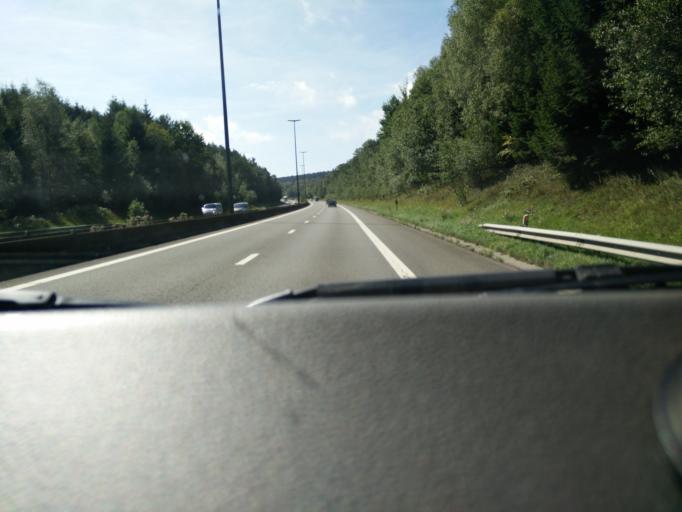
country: BE
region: Wallonia
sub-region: Province du Luxembourg
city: Tellin
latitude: 50.0272
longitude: 5.2104
